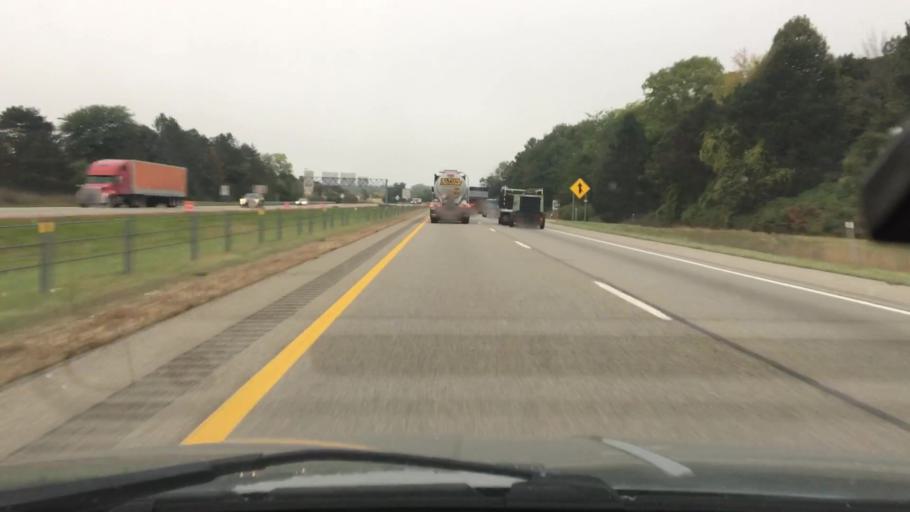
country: US
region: Michigan
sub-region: Calhoun County
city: Lakeview
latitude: 42.2669
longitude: -85.1811
